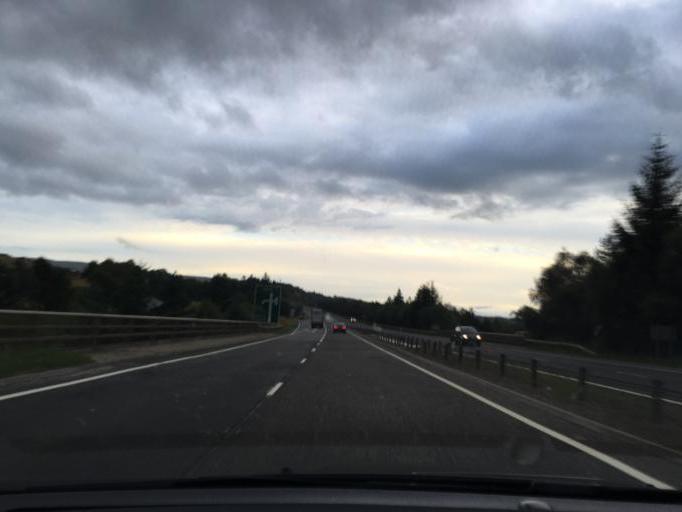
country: GB
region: Scotland
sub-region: Highland
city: Inverness
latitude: 57.4204
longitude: -4.1324
